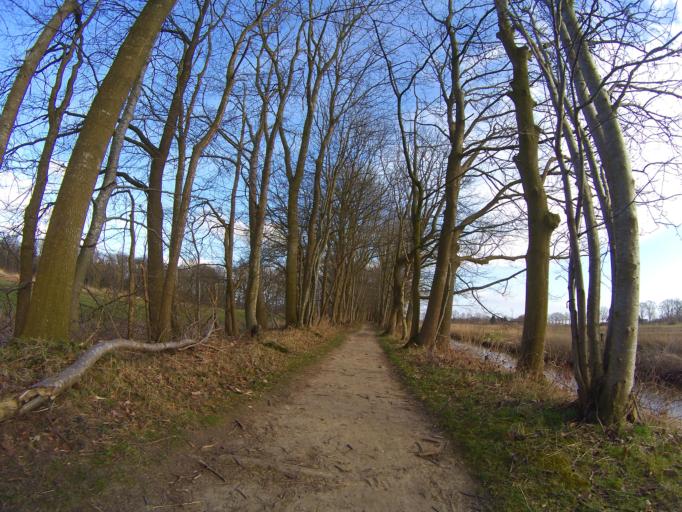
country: NL
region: Utrecht
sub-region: Gemeente Leusden
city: Leusden
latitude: 52.1529
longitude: 5.4632
